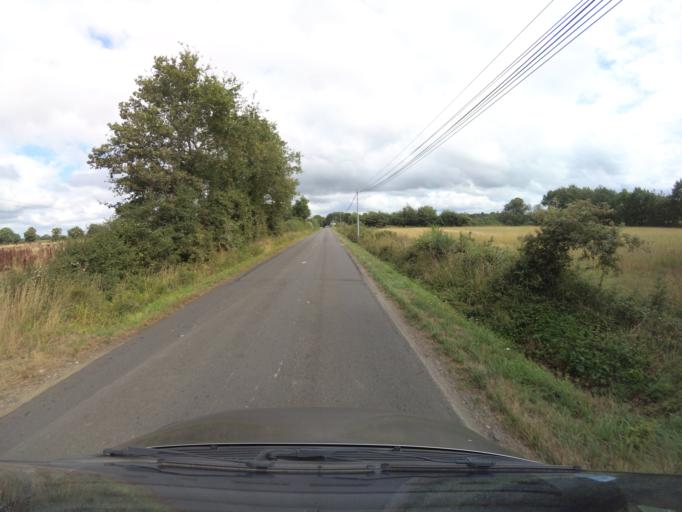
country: FR
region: Pays de la Loire
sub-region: Departement de la Loire-Atlantique
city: Saint-Philbert-de-Grand-Lieu
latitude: 47.0421
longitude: -1.6090
